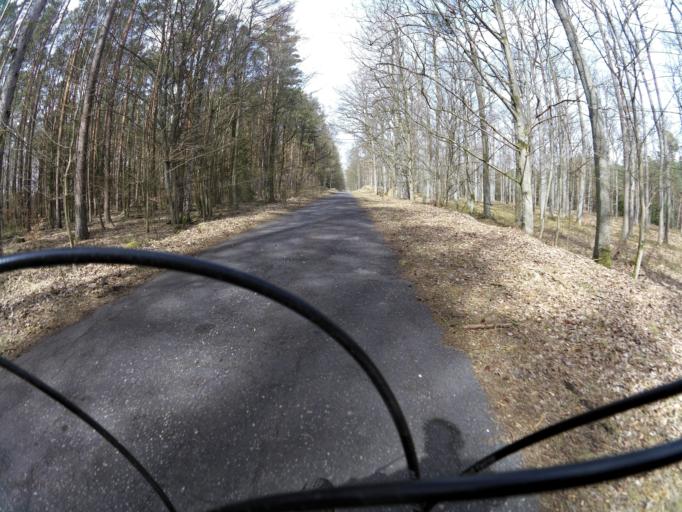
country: PL
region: West Pomeranian Voivodeship
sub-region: Powiat mysliborski
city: Boleszkowice
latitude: 52.6995
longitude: 14.5144
